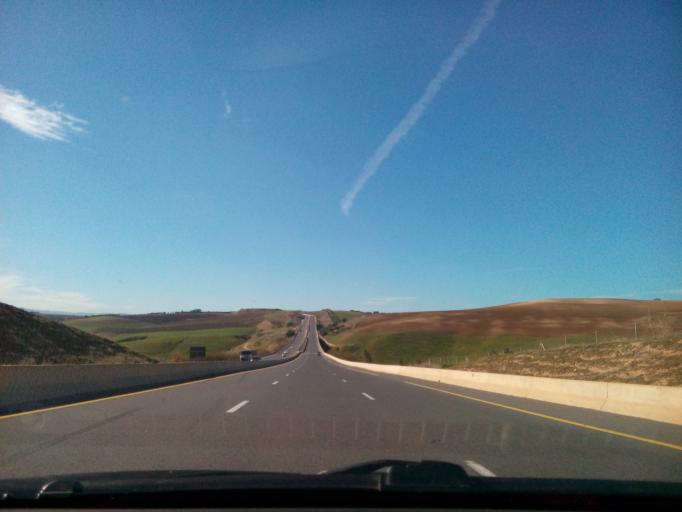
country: DZ
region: Tlemcen
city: Chetouane
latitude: 34.9843
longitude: -1.2356
